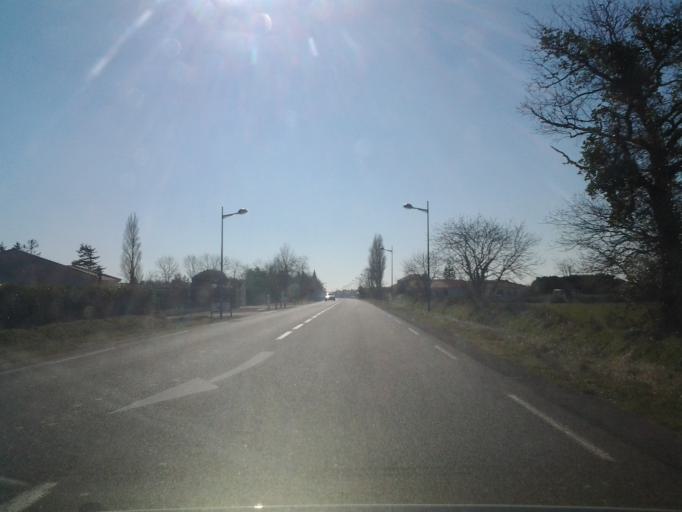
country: FR
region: Pays de la Loire
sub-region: Departement de la Vendee
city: Saint-Mathurin
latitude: 46.5711
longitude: -1.7084
